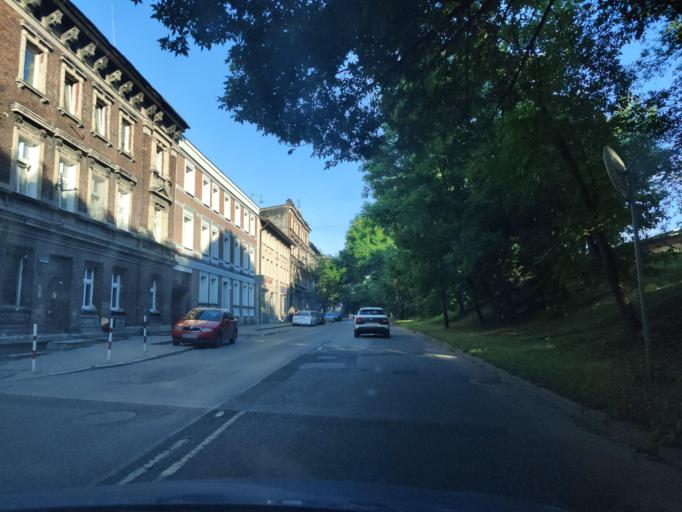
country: PL
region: Silesian Voivodeship
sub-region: Sosnowiec
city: Sosnowiec
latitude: 50.2460
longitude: 19.1335
